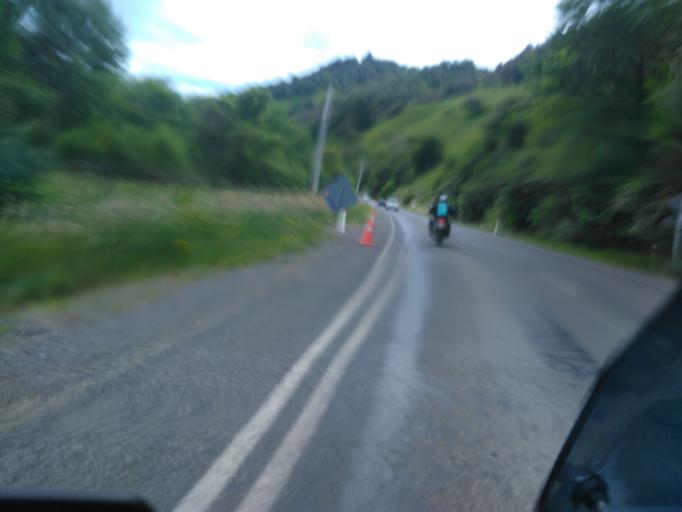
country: NZ
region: Bay of Plenty
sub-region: Opotiki District
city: Opotiki
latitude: -38.3745
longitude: 177.4864
